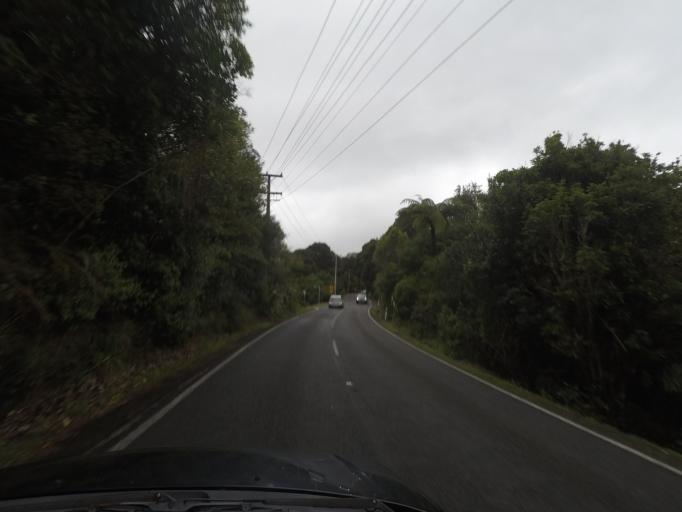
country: NZ
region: Auckland
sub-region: Auckland
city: Titirangi
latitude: -36.9319
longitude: 174.5807
